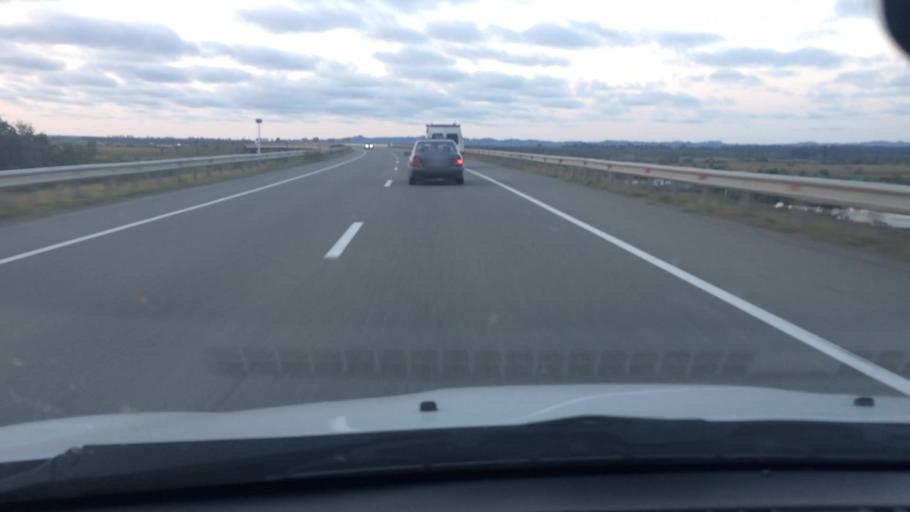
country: GE
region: Ajaria
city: Ochkhamuri
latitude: 41.8633
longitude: 41.8375
